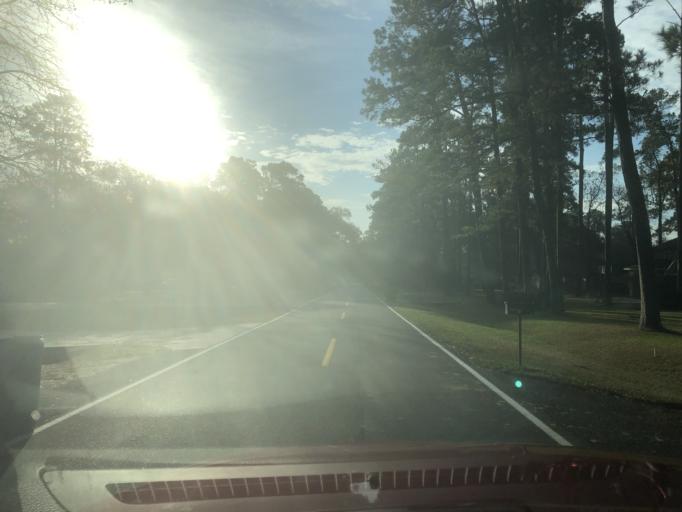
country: US
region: Texas
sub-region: Harris County
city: Spring
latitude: 30.0152
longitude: -95.4778
